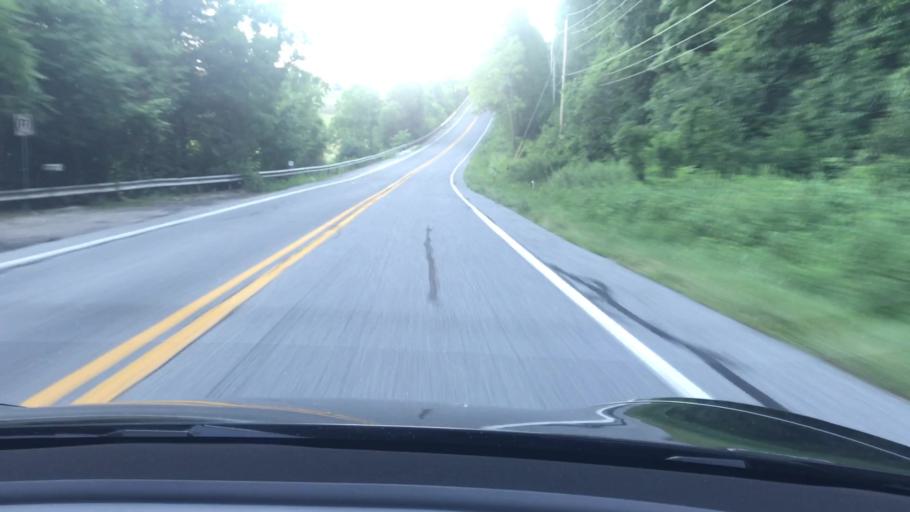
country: US
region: Pennsylvania
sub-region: York County
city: Dover
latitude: 40.0636
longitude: -76.8832
